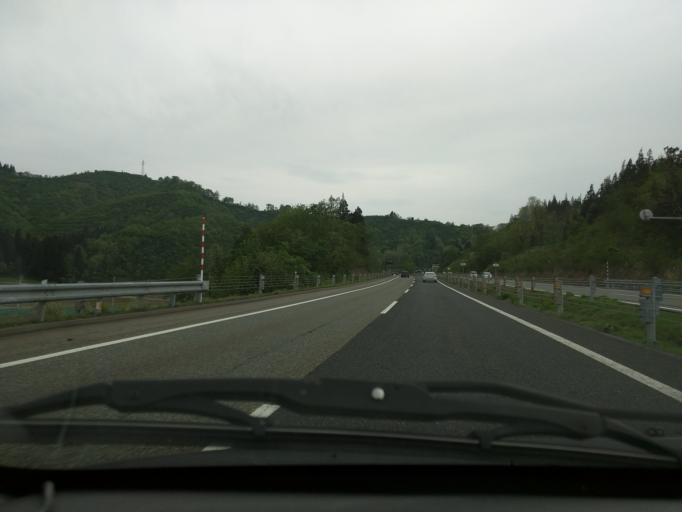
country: JP
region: Niigata
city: Muikamachi
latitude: 37.2020
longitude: 138.9639
